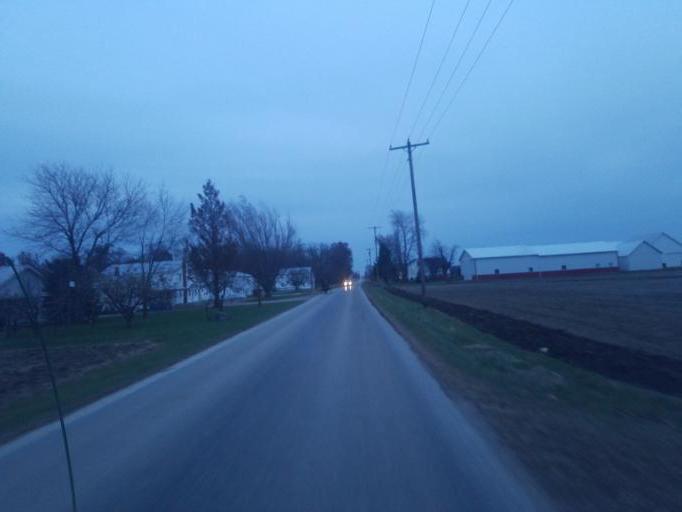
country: US
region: Indiana
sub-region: Adams County
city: Berne
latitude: 40.7315
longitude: -84.9296
